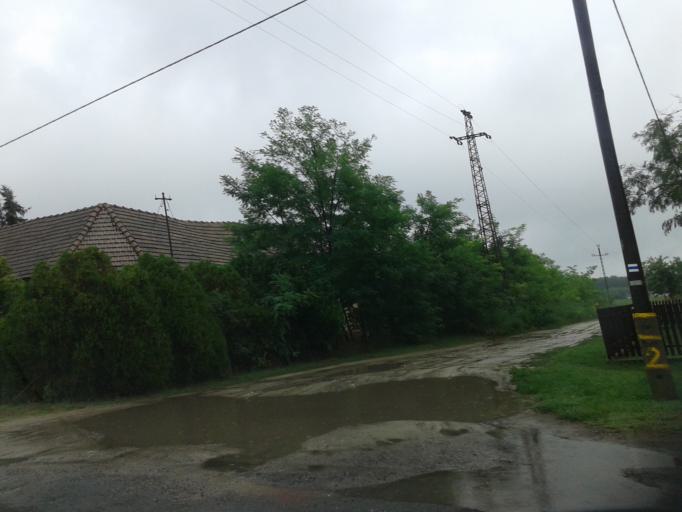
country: HU
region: Bacs-Kiskun
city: Kelebia
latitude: 46.2554
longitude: 19.6579
